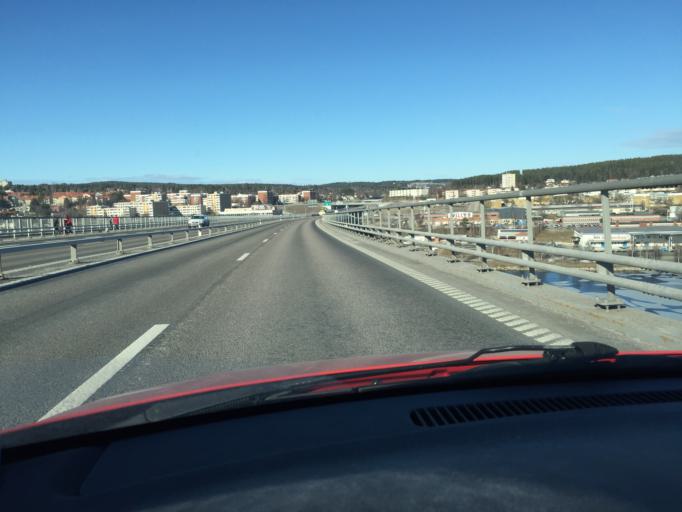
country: SE
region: Vaesternorrland
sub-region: Sundsvalls Kommun
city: Sundsvall
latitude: 62.3916
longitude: 17.3392
